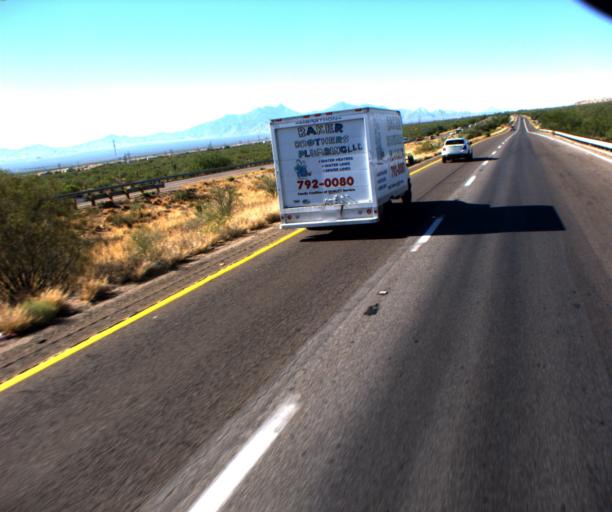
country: US
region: Arizona
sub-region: Pima County
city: Sahuarita
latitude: 32.0003
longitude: -110.9924
